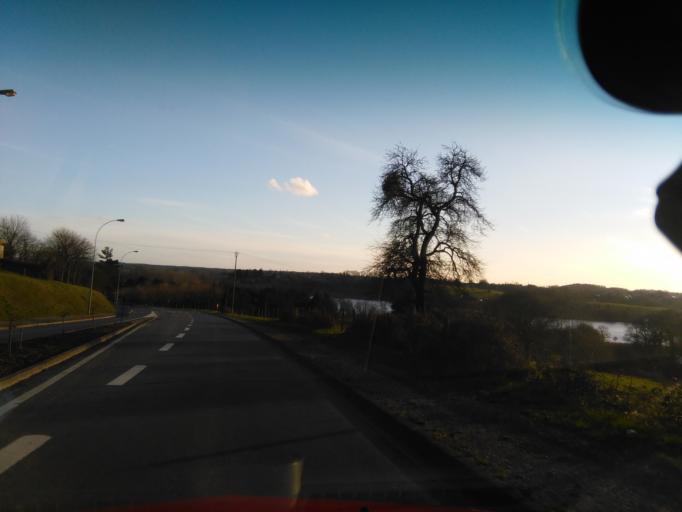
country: FR
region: Lower Normandy
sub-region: Departement de l'Orne
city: La Ferte-Mace
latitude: 48.5940
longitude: -0.3662
